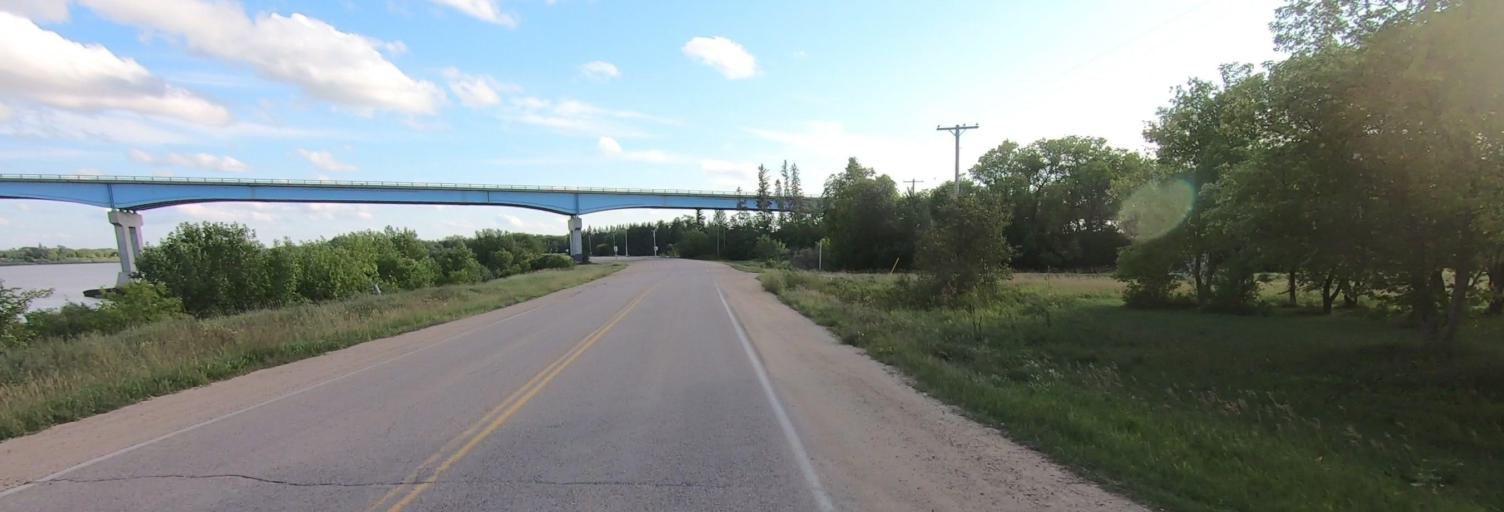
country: CA
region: Manitoba
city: Selkirk
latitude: 50.1929
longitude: -96.8442
